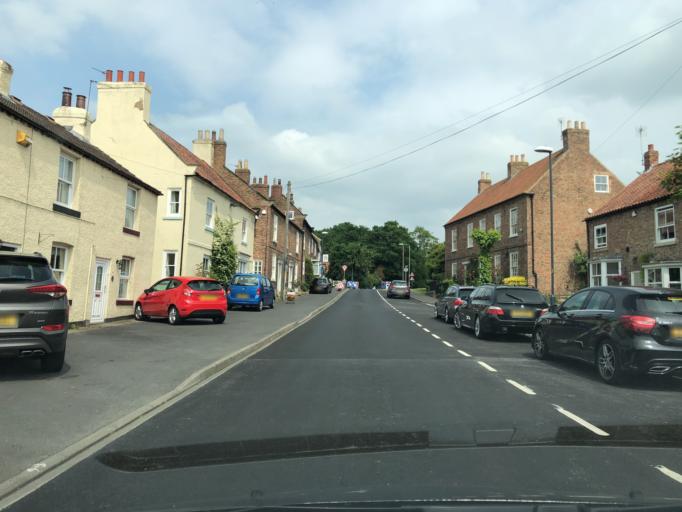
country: GB
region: England
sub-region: North Yorkshire
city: Thirsk
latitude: 54.1787
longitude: -1.3876
